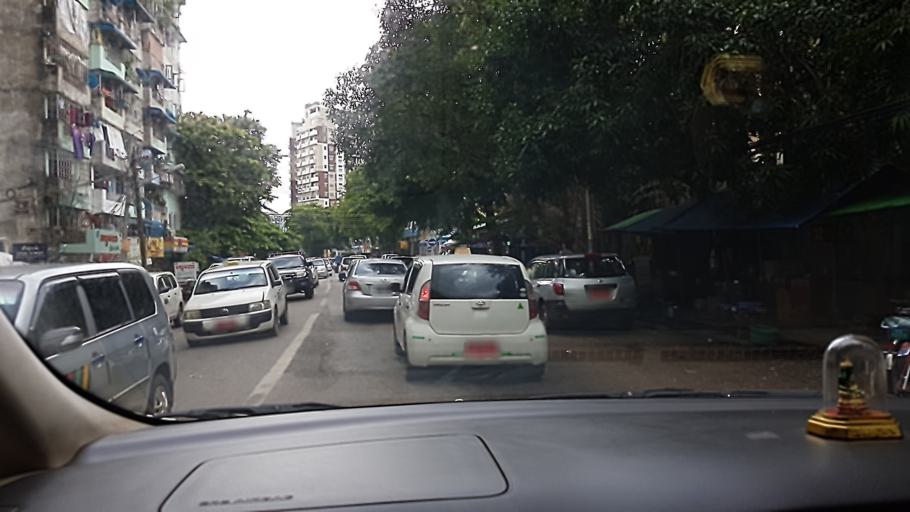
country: MM
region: Yangon
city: Yangon
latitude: 16.8025
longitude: 96.1299
